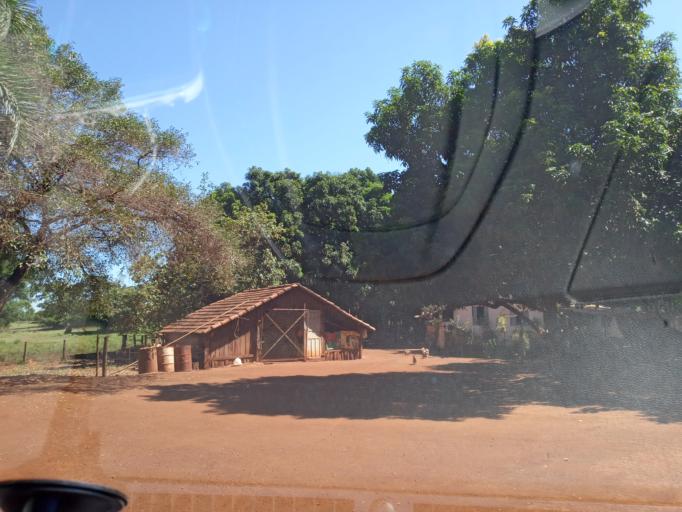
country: BR
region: Goias
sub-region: Itumbiara
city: Itumbiara
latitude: -18.4459
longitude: -49.1542
